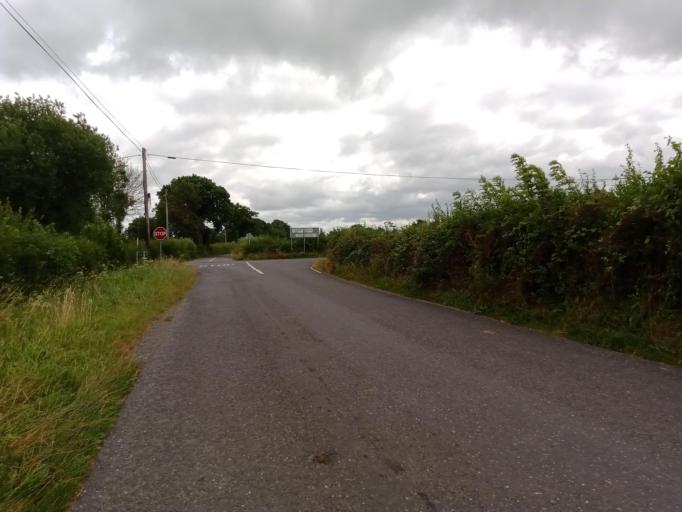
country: IE
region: Leinster
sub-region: Kilkenny
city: Callan
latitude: 52.5760
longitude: -7.3783
